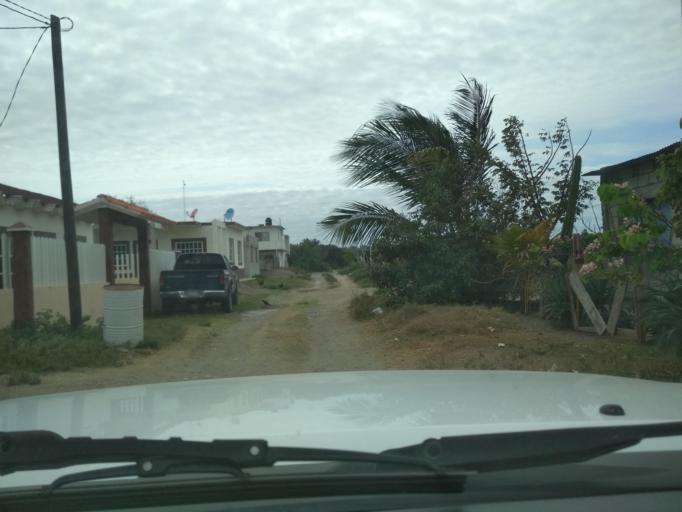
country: MX
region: Veracruz
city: Anton Lizardo
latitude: 19.0359
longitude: -95.9705
